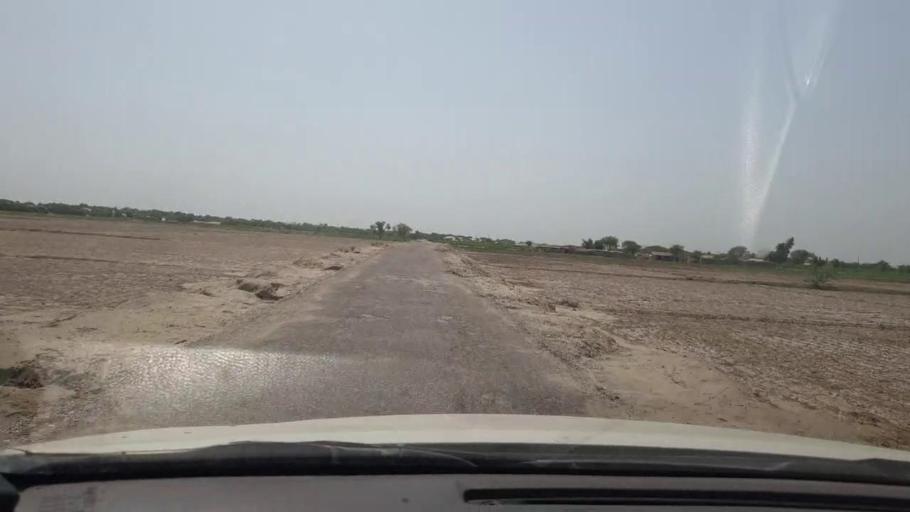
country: PK
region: Sindh
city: Rohri
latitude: 27.5184
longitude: 69.0852
